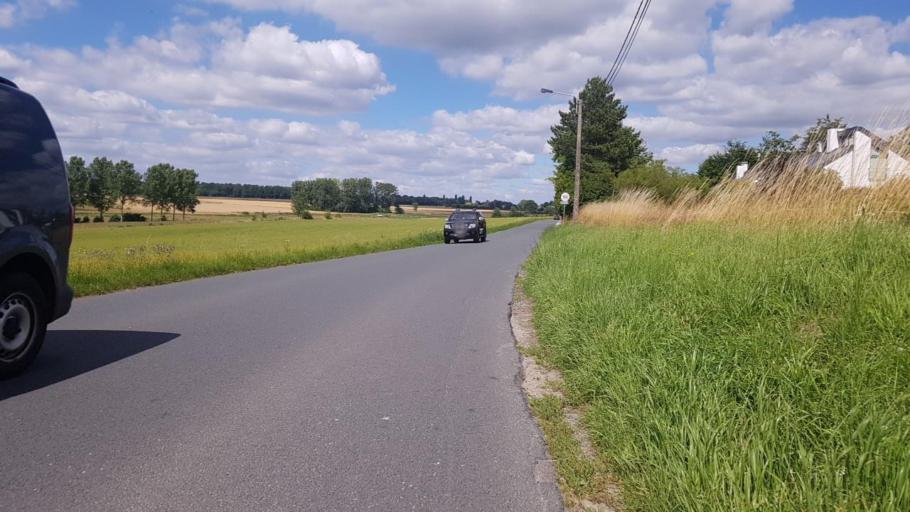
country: BE
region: Wallonia
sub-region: Province de Namur
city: Walcourt
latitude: 50.3288
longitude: 4.3810
